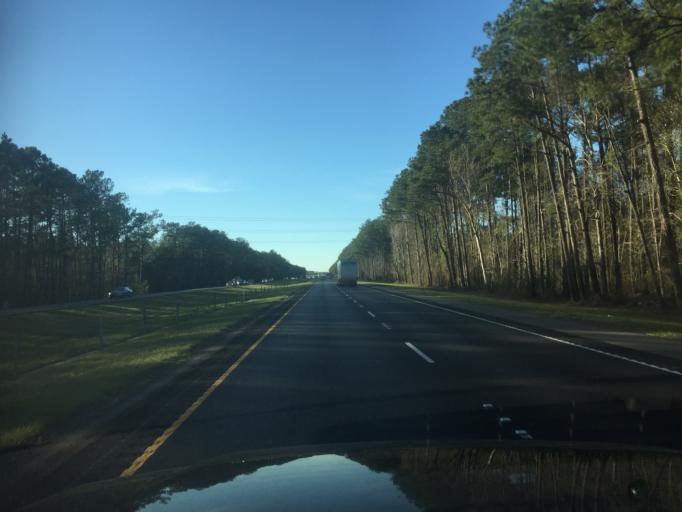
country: US
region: Louisiana
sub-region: Saint Tammany Parish
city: Lacombe
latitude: 30.3844
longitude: -89.9840
